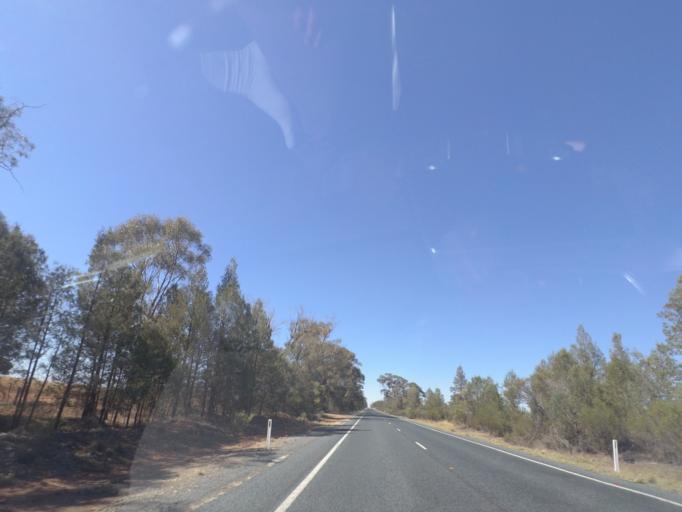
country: AU
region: New South Wales
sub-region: Bland
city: West Wyalong
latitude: -34.1523
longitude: 147.1182
